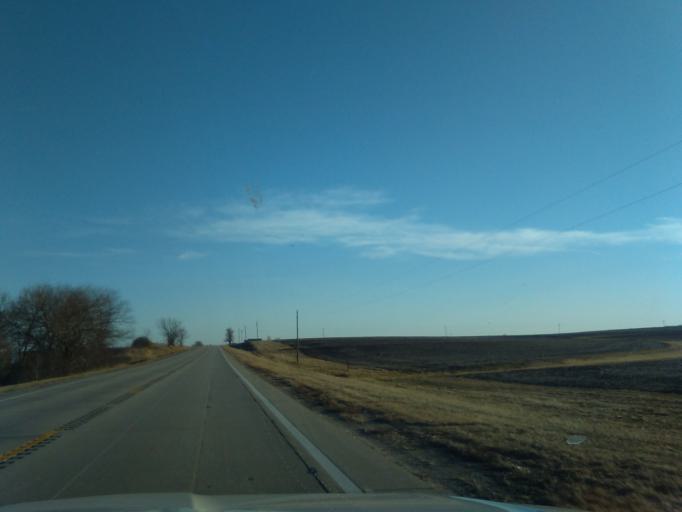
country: US
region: Nebraska
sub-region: Johnson County
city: Tecumseh
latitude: 40.4838
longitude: -96.1799
